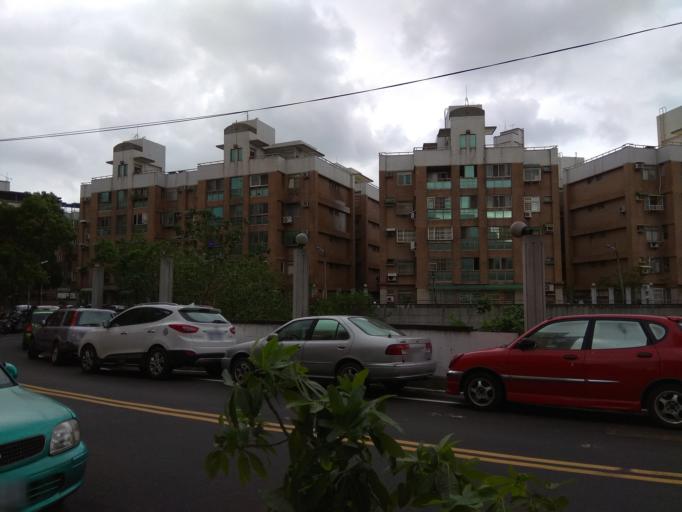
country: TW
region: Taiwan
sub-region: Hsinchu
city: Hsinchu
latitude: 24.7636
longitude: 120.9782
